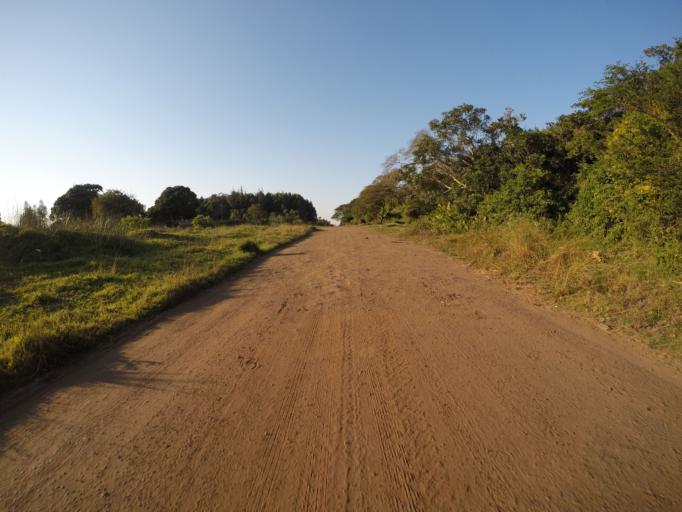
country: ZA
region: KwaZulu-Natal
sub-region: uThungulu District Municipality
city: KwaMbonambi
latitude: -28.6993
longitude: 32.1933
